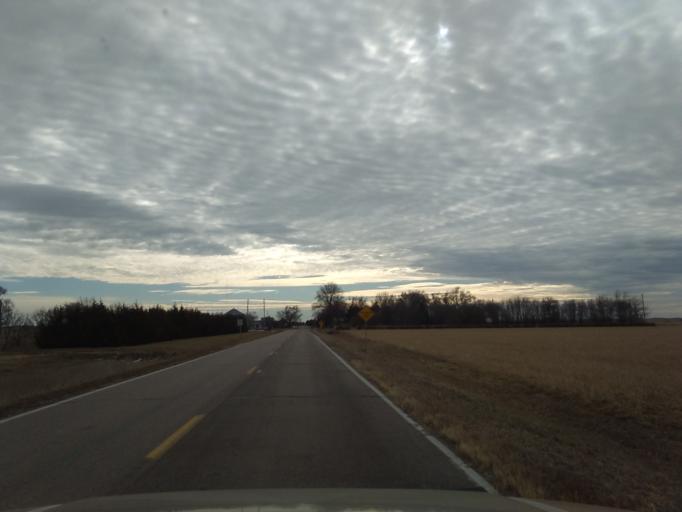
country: US
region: Nebraska
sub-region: Buffalo County
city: Gibbon
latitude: 40.6498
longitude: -98.8473
